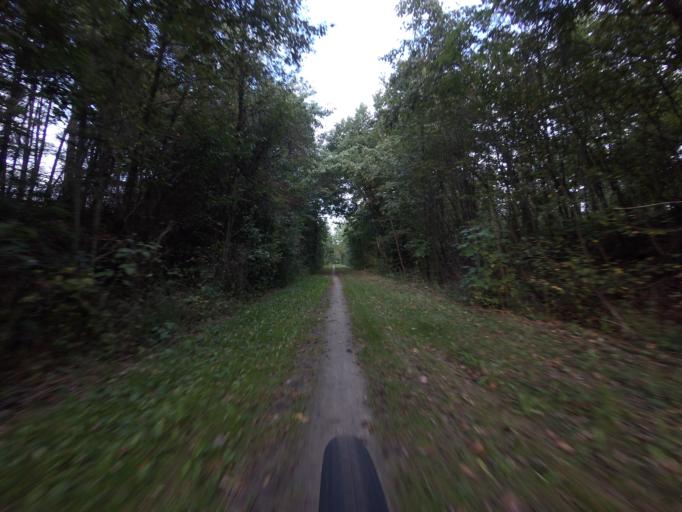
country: DK
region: Central Jutland
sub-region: Ikast-Brande Kommune
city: Brande
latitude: 55.8799
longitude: 9.0487
